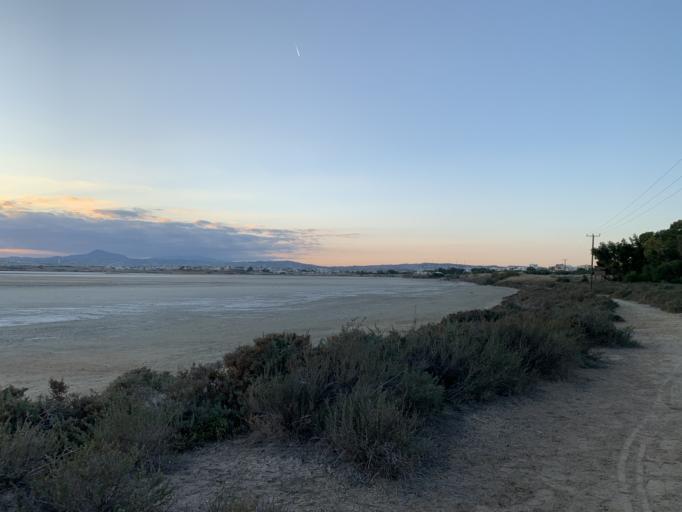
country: CY
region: Larnaka
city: Larnaca
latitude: 34.9050
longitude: 33.6215
